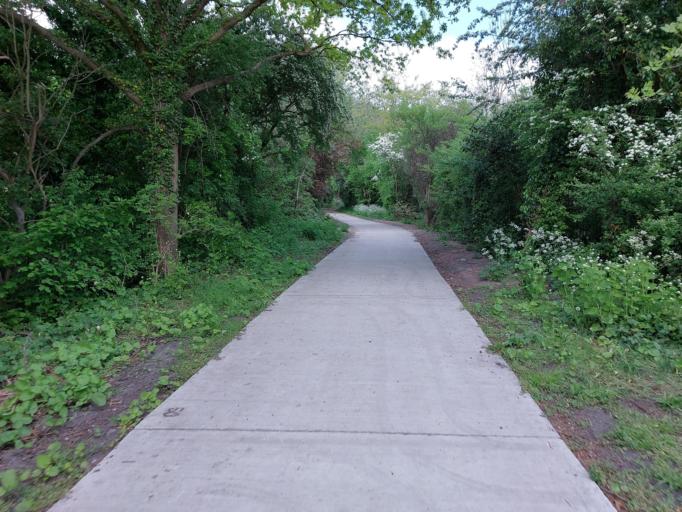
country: BE
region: Wallonia
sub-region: Province du Hainaut
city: Frameries
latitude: 50.3993
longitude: 3.9039
